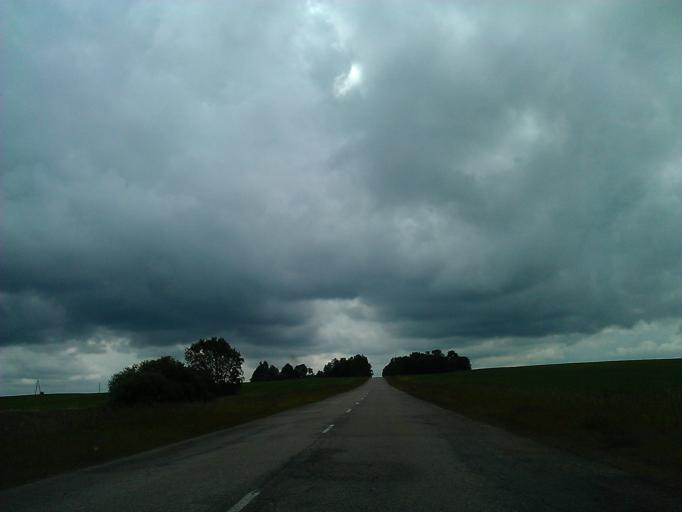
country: LV
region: Aizpute
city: Aizpute
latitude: 56.8354
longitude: 21.7570
